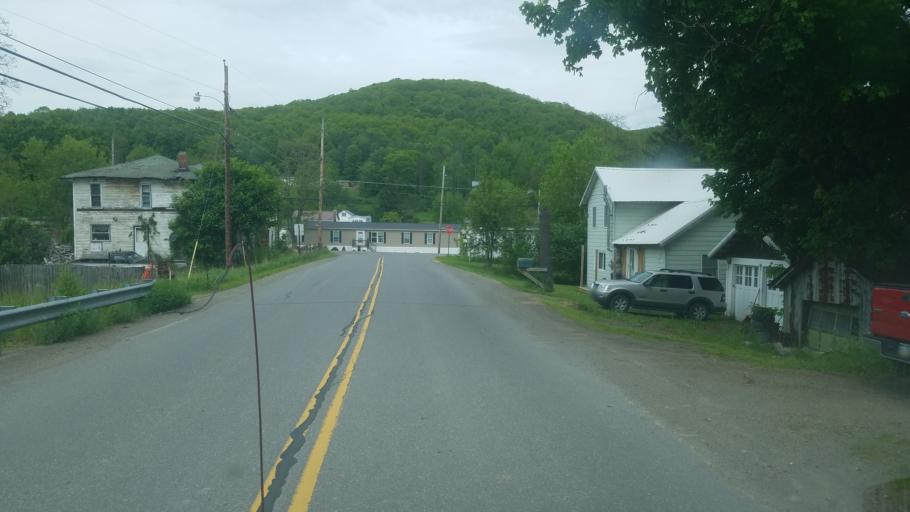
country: US
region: Pennsylvania
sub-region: Tioga County
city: Westfield
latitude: 41.9128
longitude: -77.6038
